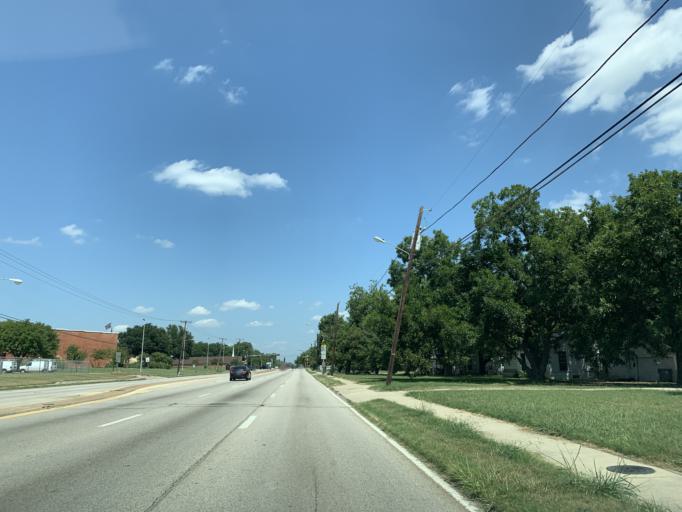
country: US
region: Texas
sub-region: Dallas County
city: Hutchins
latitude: 32.6892
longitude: -96.7827
